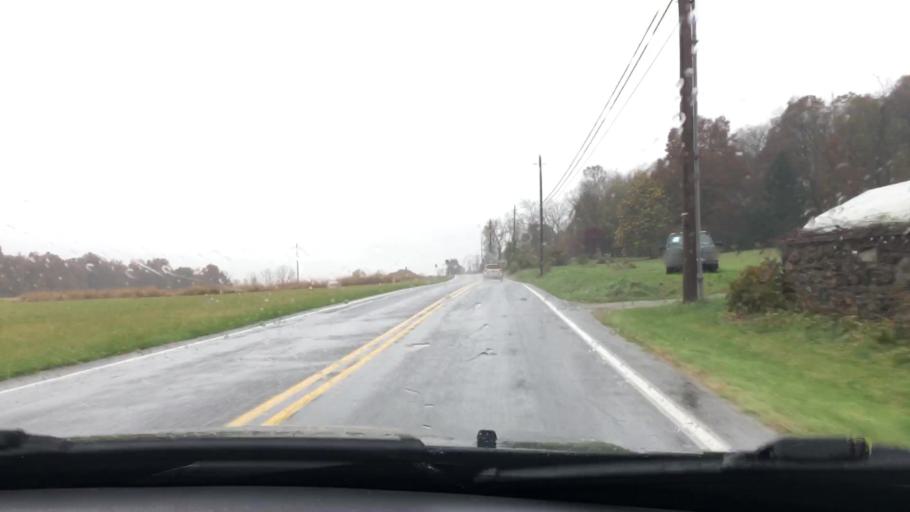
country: US
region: Pennsylvania
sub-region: York County
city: Glen Rock
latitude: 39.7448
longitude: -76.8092
